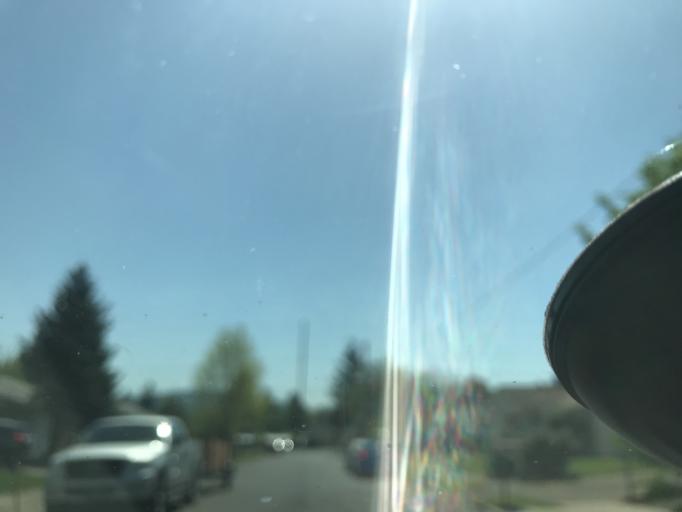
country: US
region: Oregon
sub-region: Multnomah County
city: Lents
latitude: 45.4909
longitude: -122.5583
